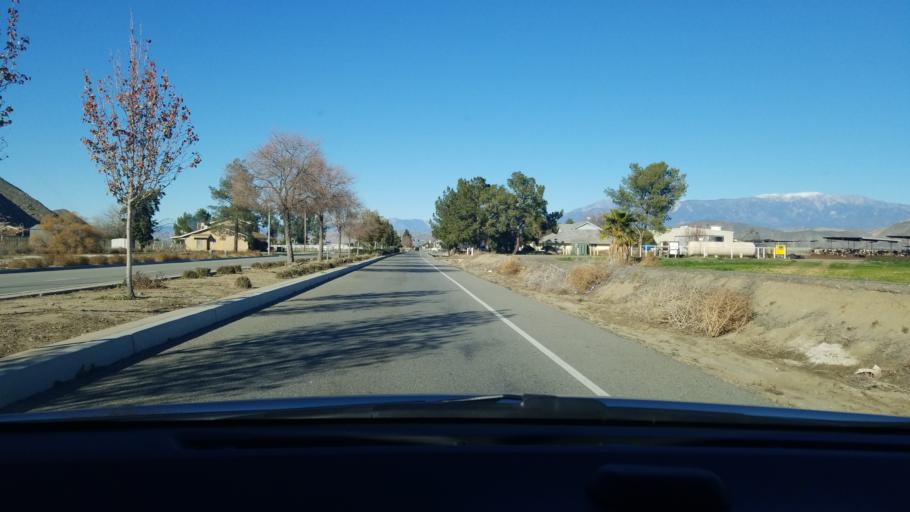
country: US
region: California
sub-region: Riverside County
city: Green Acres
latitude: 33.7939
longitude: -117.0337
